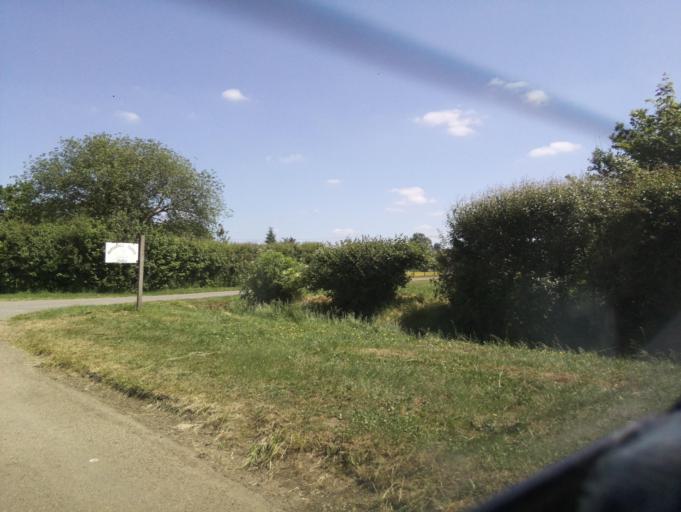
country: GB
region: England
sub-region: Wiltshire
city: Bremhill
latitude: 51.4773
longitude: -2.0444
